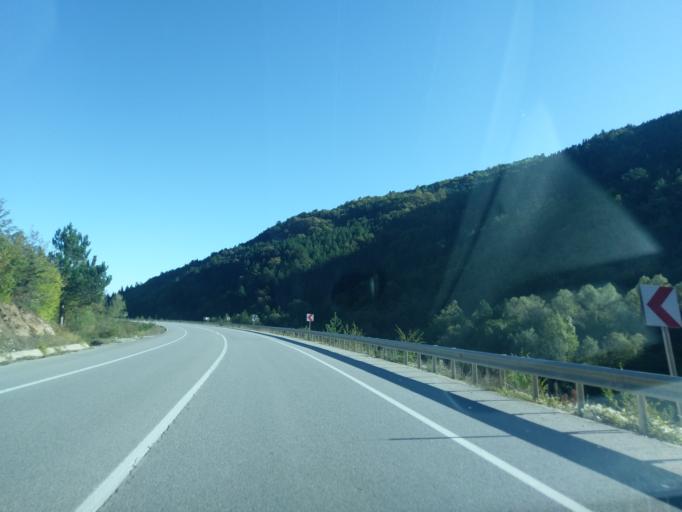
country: TR
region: Sinop
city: Erfelek
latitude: 41.7131
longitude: 34.9326
